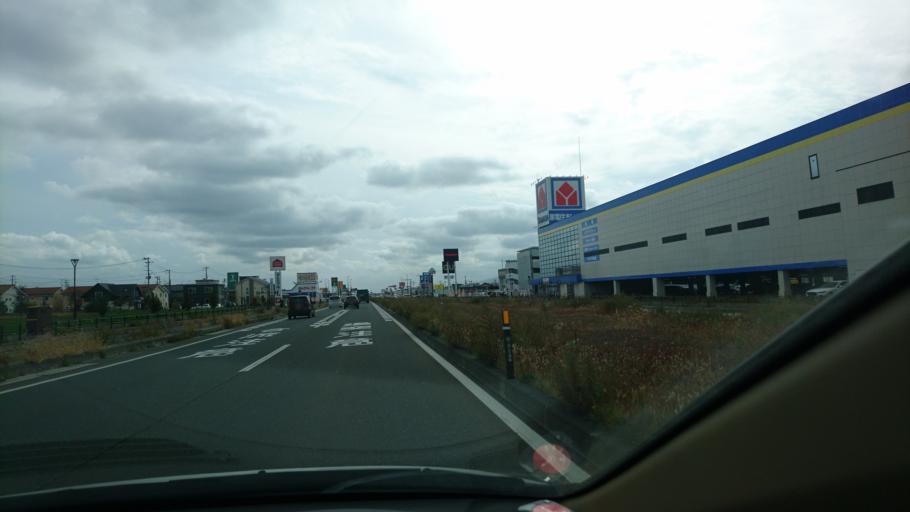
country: JP
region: Iwate
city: Morioka-shi
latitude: 39.6796
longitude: 141.1354
